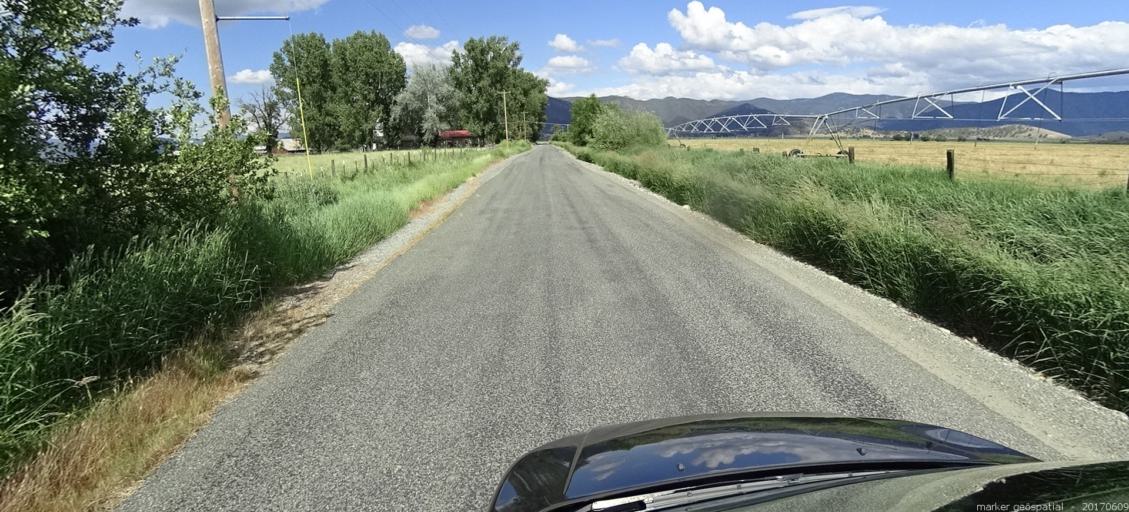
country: US
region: California
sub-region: Siskiyou County
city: Yreka
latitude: 41.4967
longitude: -122.8846
